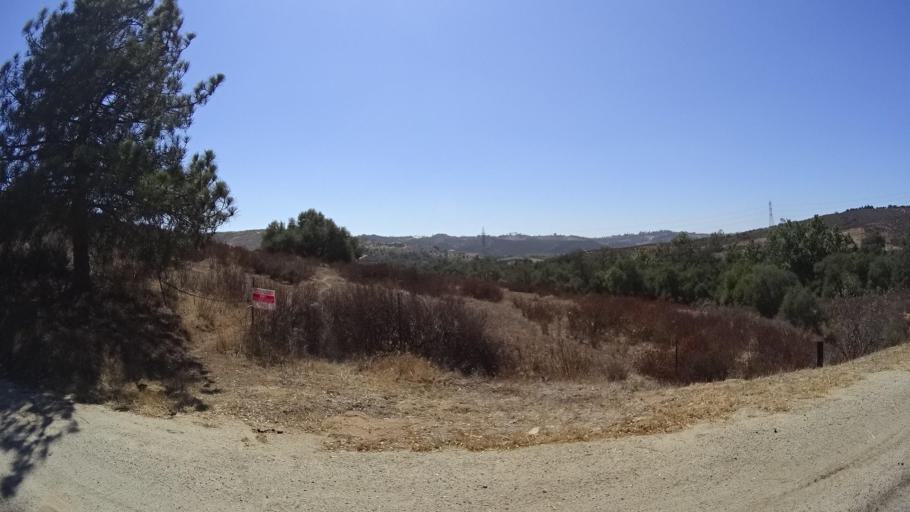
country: US
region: California
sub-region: San Diego County
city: Hidden Meadows
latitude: 33.2924
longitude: -117.0864
